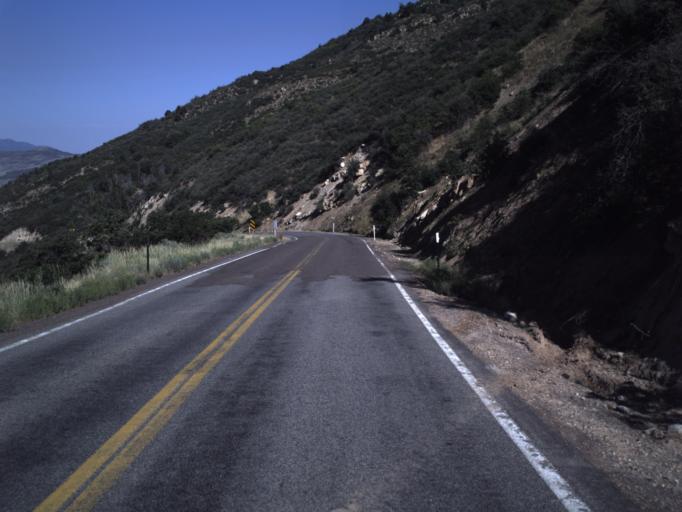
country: US
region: Utah
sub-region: Sanpete County
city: Fairview
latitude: 39.6486
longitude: -111.3833
